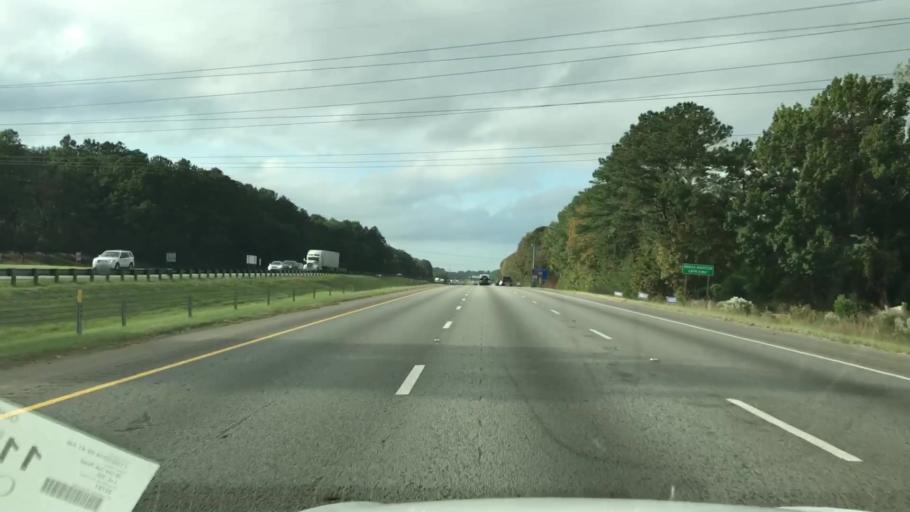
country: US
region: South Carolina
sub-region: Berkeley County
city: Ladson
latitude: 32.9905
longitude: -80.0851
